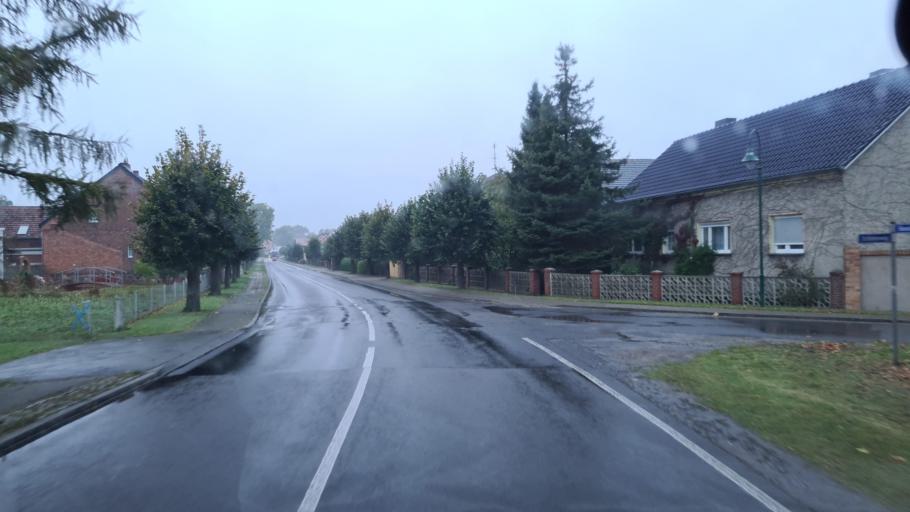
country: DE
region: Brandenburg
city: Rietz Neuendorf
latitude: 52.2127
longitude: 14.2138
